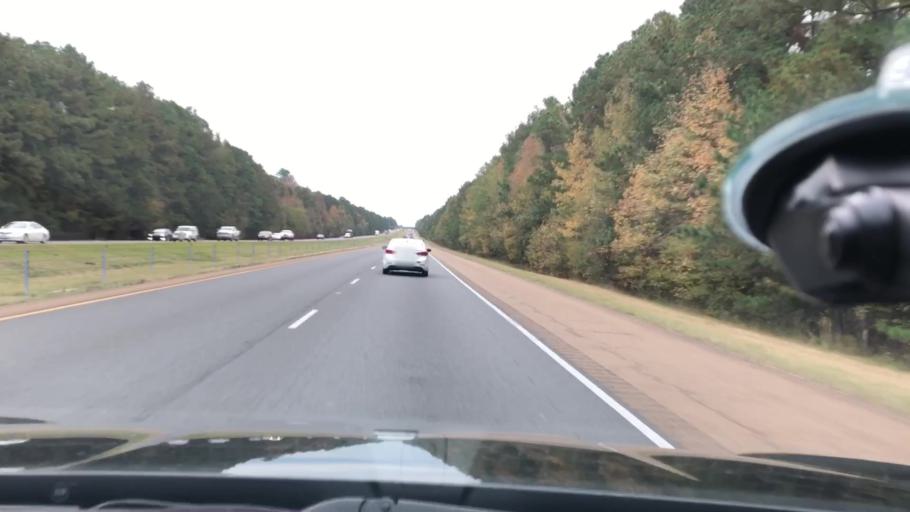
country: US
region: Arkansas
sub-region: Clark County
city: Gurdon
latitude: 33.9618
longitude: -93.2183
